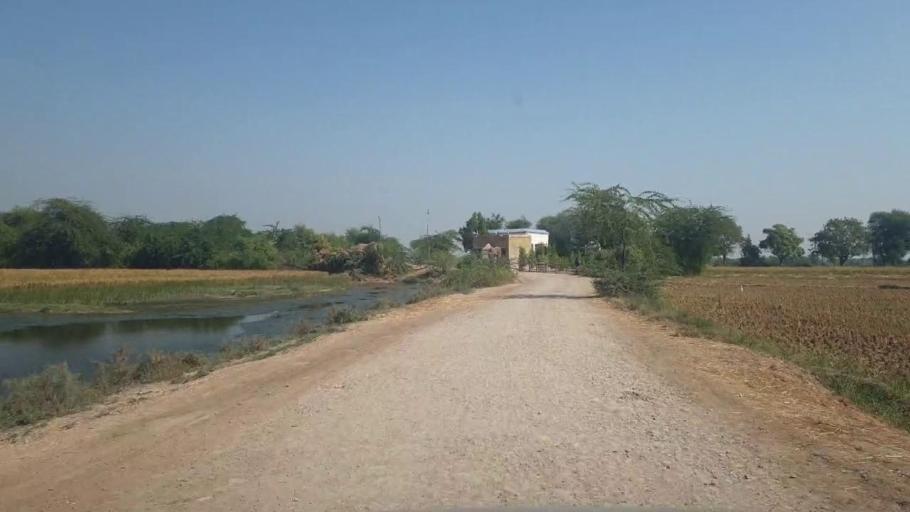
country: PK
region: Sindh
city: Badin
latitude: 24.6764
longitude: 68.8572
